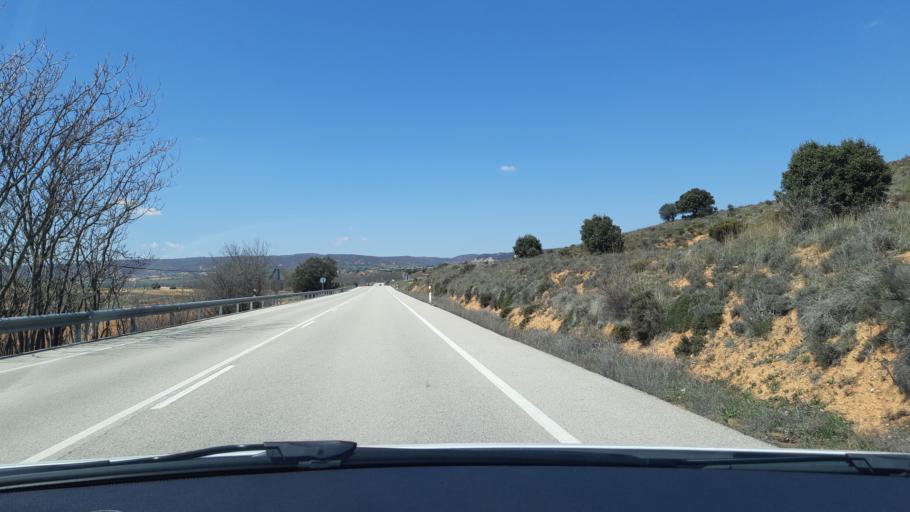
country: ES
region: Castille-La Mancha
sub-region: Provincia de Guadalajara
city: Masegoso de Tajuna
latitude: 40.8123
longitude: -2.6840
